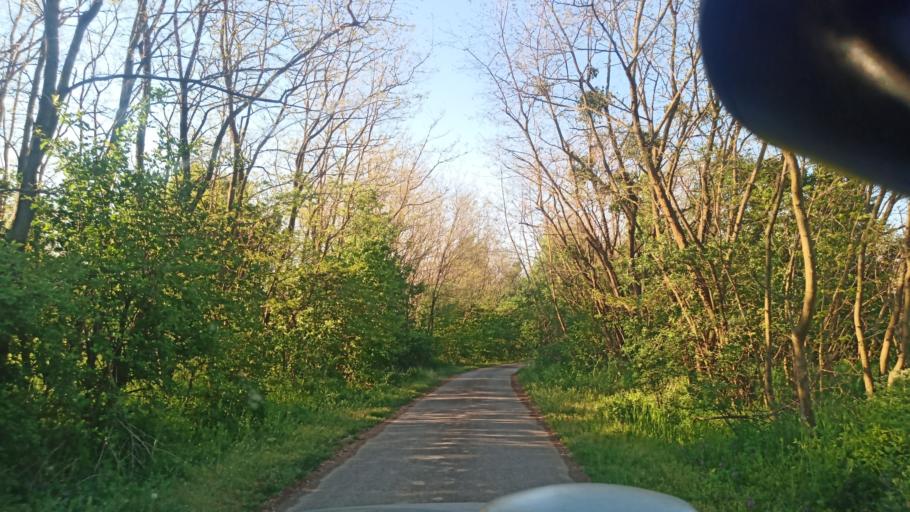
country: HU
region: Zala
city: Sarmellek
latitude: 46.7195
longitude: 17.0959
